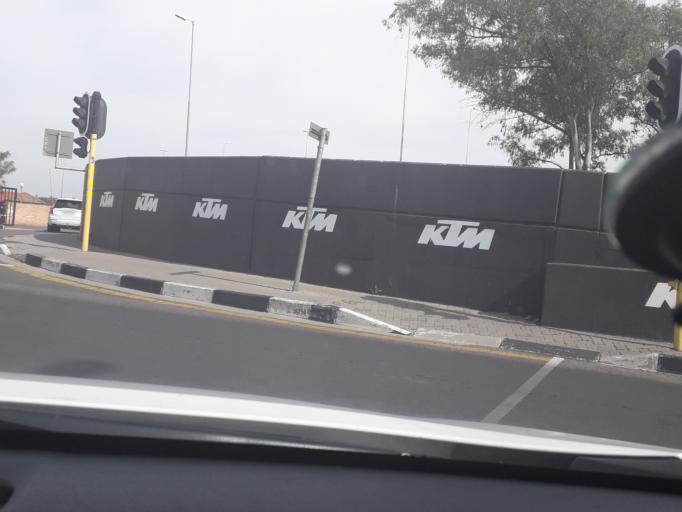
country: ZA
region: Gauteng
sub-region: City of Johannesburg Metropolitan Municipality
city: Midrand
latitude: -26.0377
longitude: 28.0625
